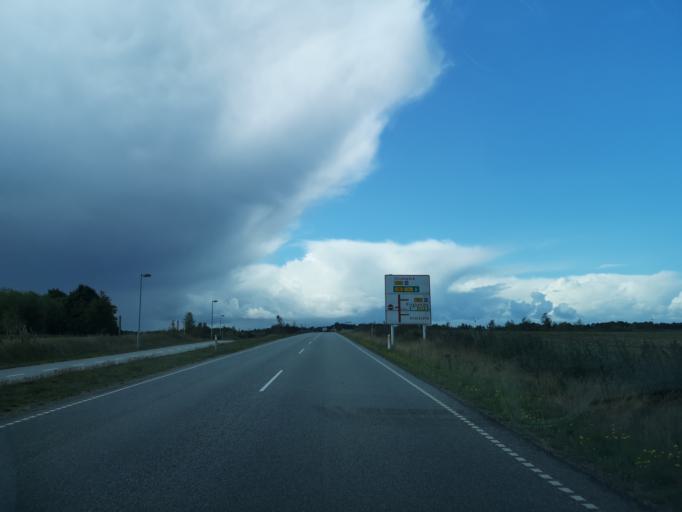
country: DK
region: Central Jutland
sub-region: Herning Kommune
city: Snejbjerg
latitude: 56.1214
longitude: 8.9122
